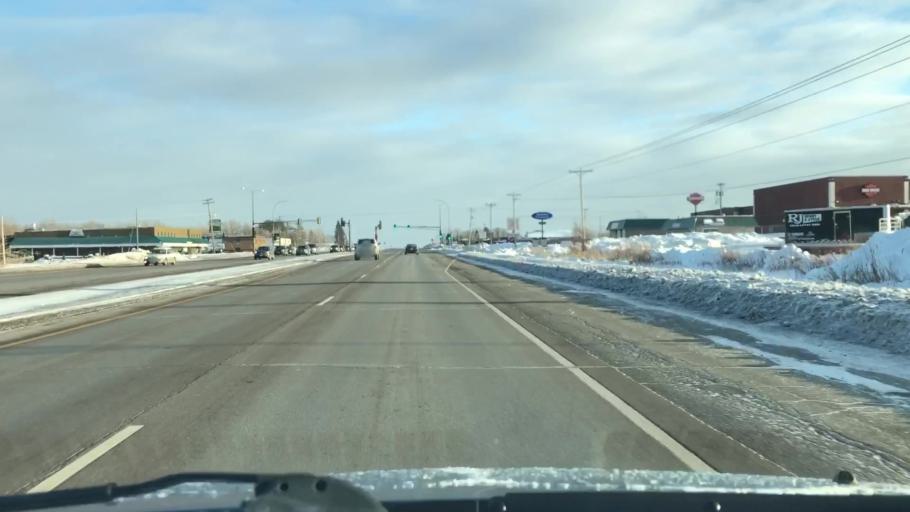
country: US
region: Minnesota
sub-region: Saint Louis County
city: Hermantown
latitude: 46.8287
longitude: -92.1977
